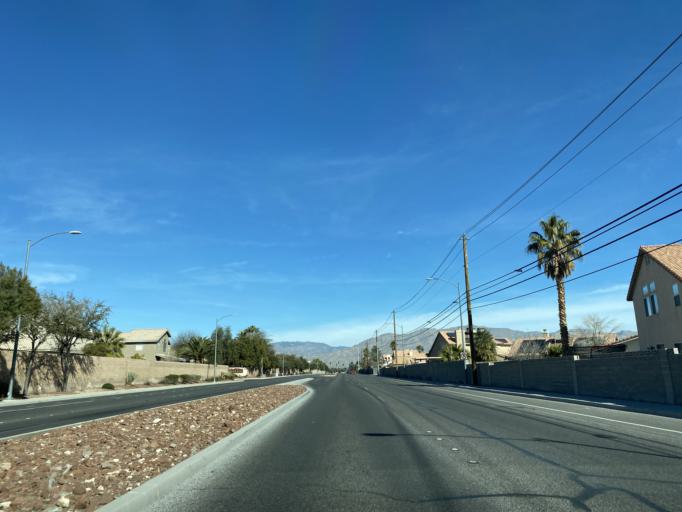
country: US
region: Nevada
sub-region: Clark County
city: Las Vegas
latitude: 36.2578
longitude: -115.2254
